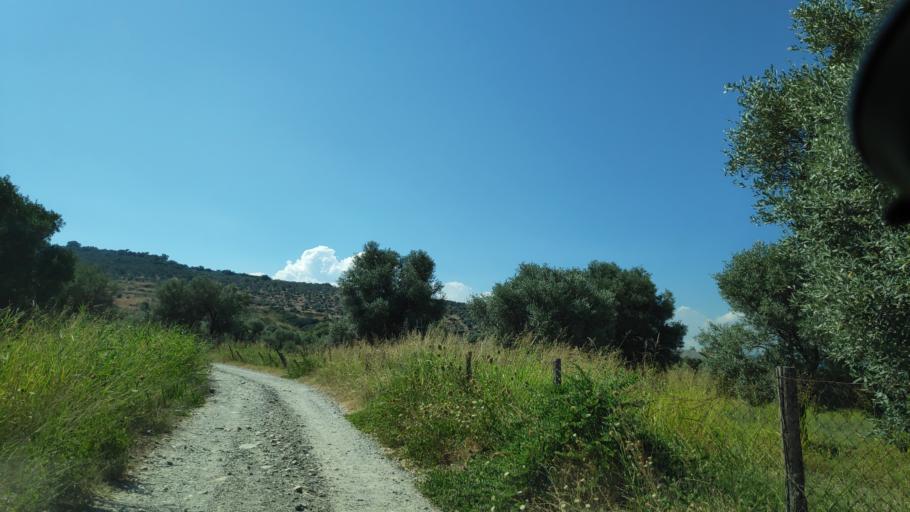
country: IT
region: Calabria
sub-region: Provincia di Reggio Calabria
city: Monasterace
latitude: 38.4360
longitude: 16.5279
